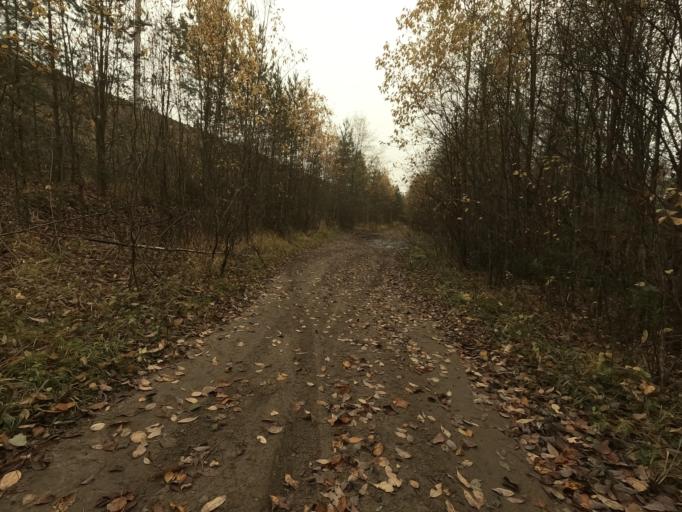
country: RU
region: Leningrad
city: Pavlovo
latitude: 59.7767
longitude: 30.9004
